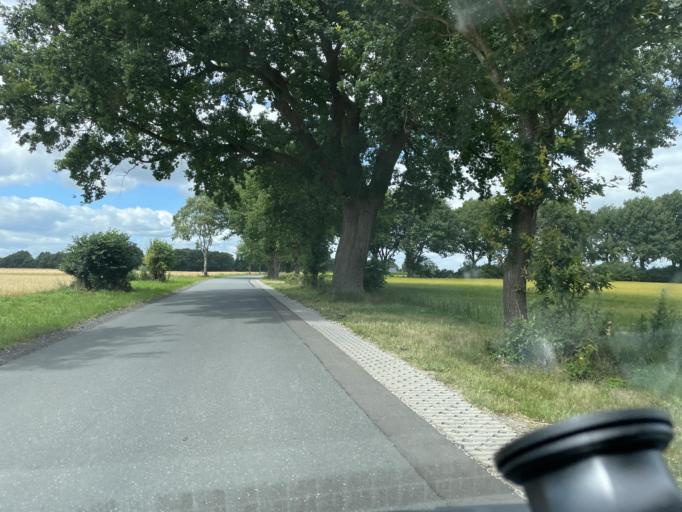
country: DE
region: Lower Saxony
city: Buxtehude
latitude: 53.4508
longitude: 9.7145
